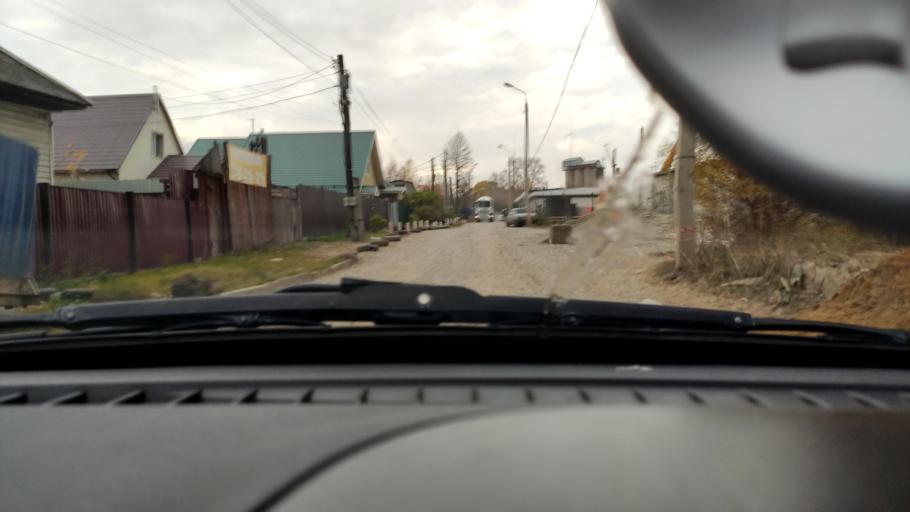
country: RU
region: Perm
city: Perm
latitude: 57.9736
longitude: 56.1887
